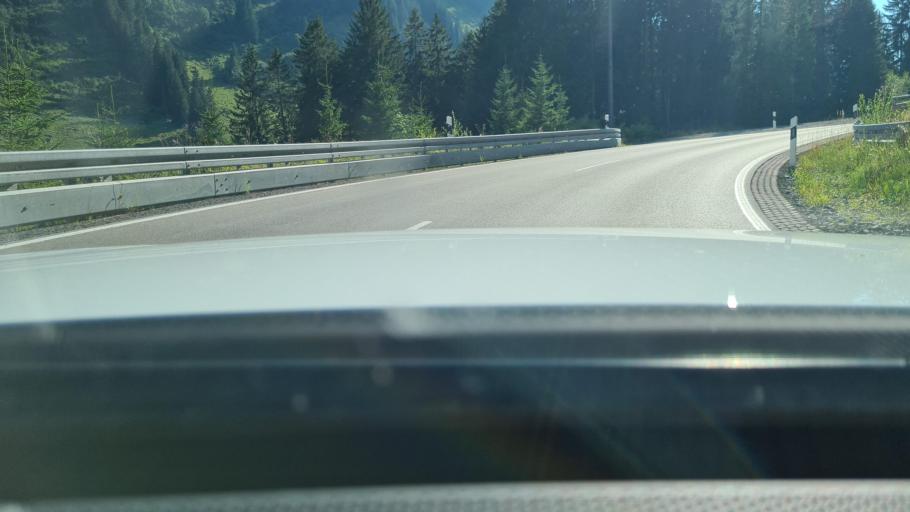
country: DE
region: Bavaria
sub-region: Swabia
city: Obermaiselstein
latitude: 47.4334
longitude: 10.1931
